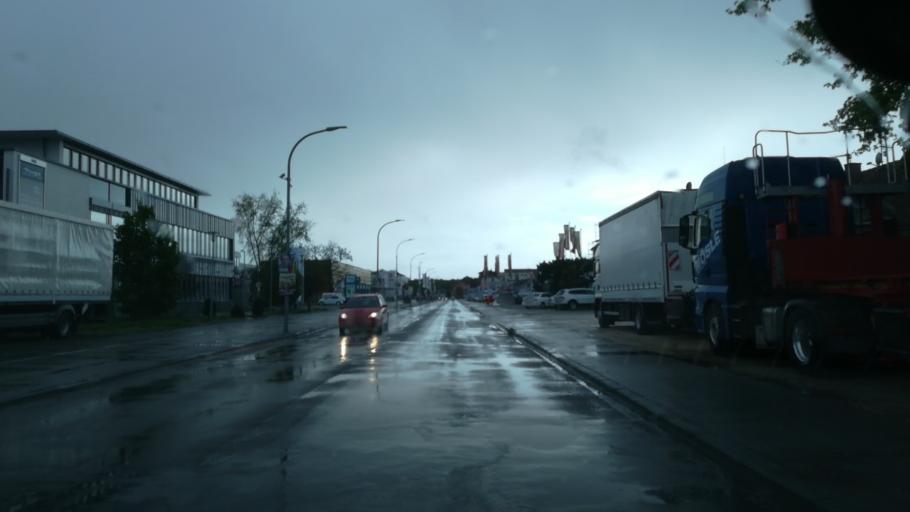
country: DE
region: Baden-Wuerttemberg
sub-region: Freiburg Region
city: Singen
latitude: 47.7495
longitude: 8.8502
